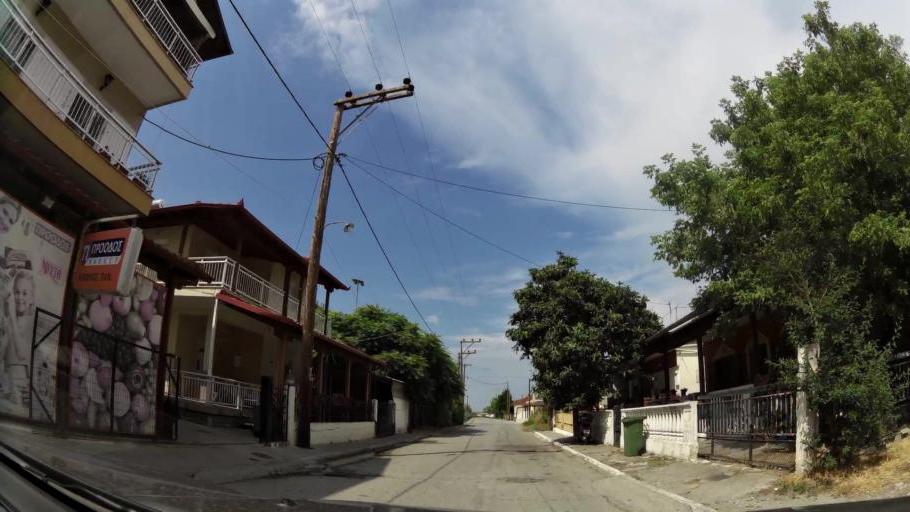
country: GR
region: Central Macedonia
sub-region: Nomos Pierias
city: Korinos
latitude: 40.3200
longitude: 22.5869
